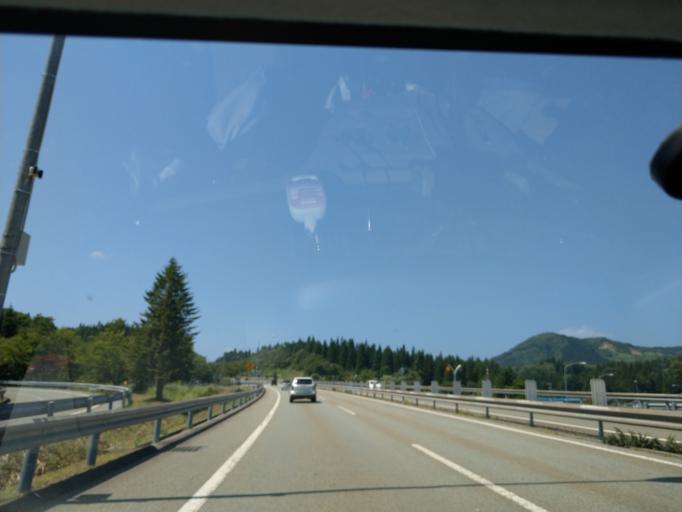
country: JP
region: Akita
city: Omagari
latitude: 39.4261
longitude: 140.4272
